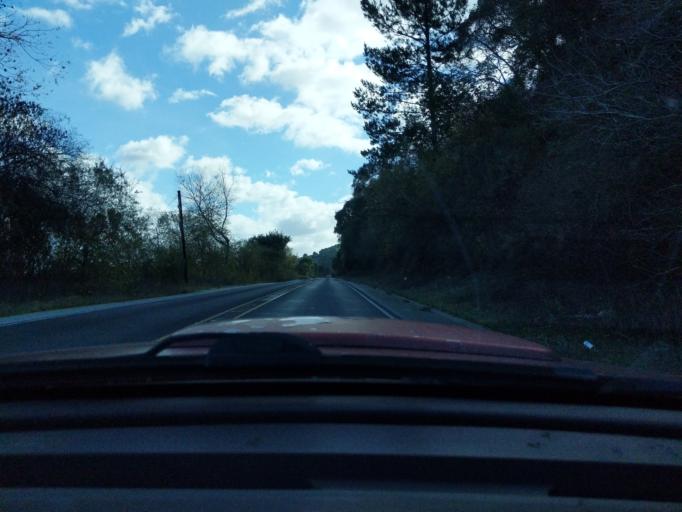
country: US
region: California
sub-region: San Benito County
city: Aromas
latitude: 36.8981
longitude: -121.5833
